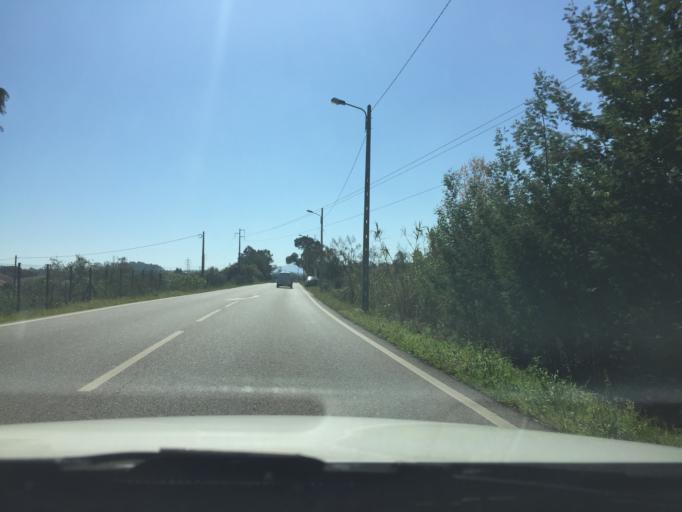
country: PT
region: Aveiro
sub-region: Anadia
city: Arcos
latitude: 40.4468
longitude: -8.4617
